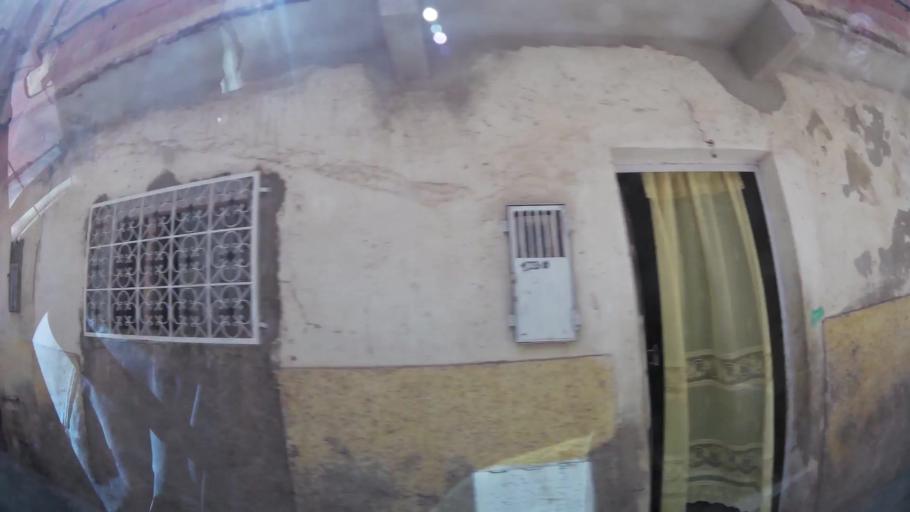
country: MA
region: Oriental
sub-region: Oujda-Angad
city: Oujda
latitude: 34.6565
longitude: -1.9222
